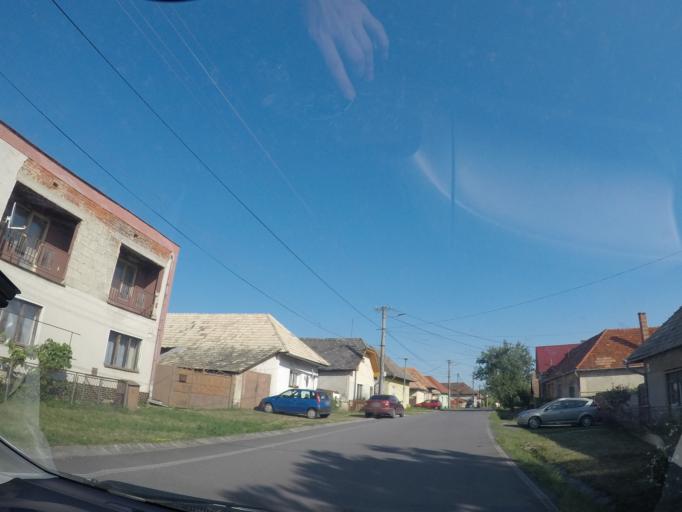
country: SK
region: Banskobystricky
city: Dudince
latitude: 48.1857
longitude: 18.8447
